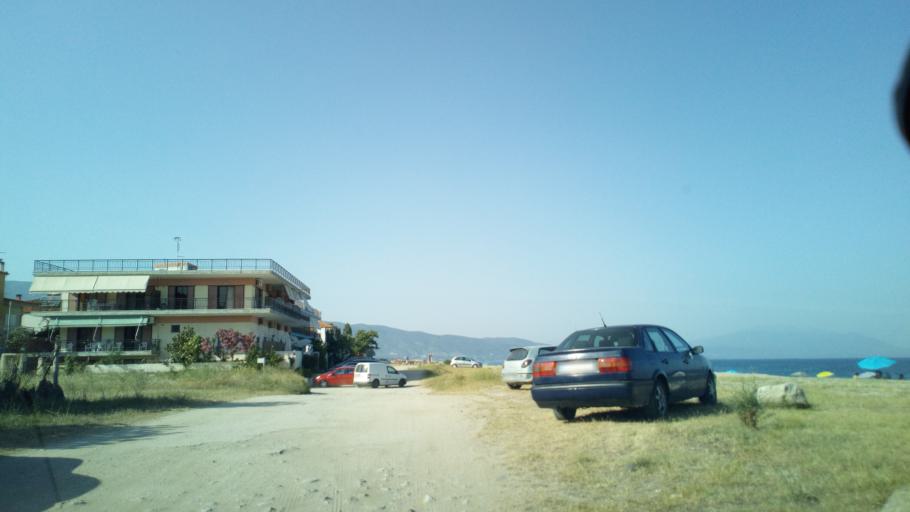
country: GR
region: Central Macedonia
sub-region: Nomos Thessalonikis
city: Nea Vrasna
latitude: 40.7018
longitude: 23.6996
